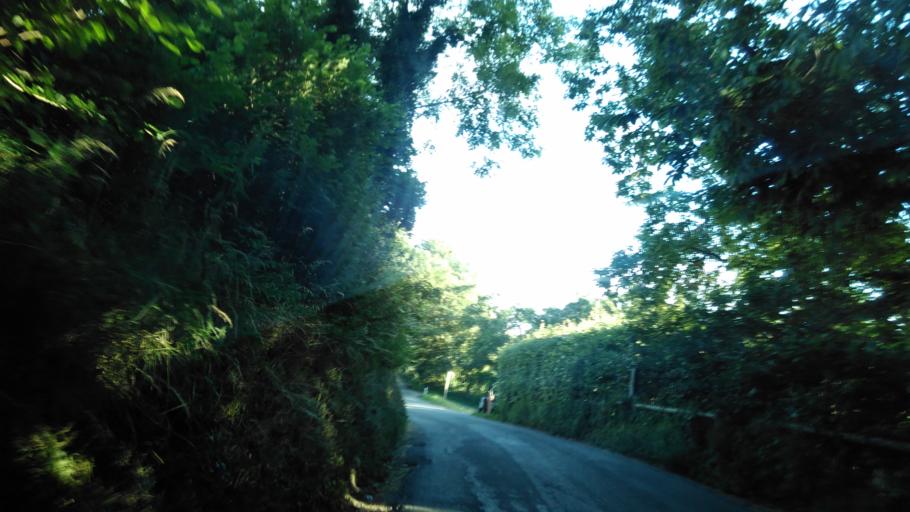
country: GB
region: England
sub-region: Kent
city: Chartham
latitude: 51.2785
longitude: 1.0103
